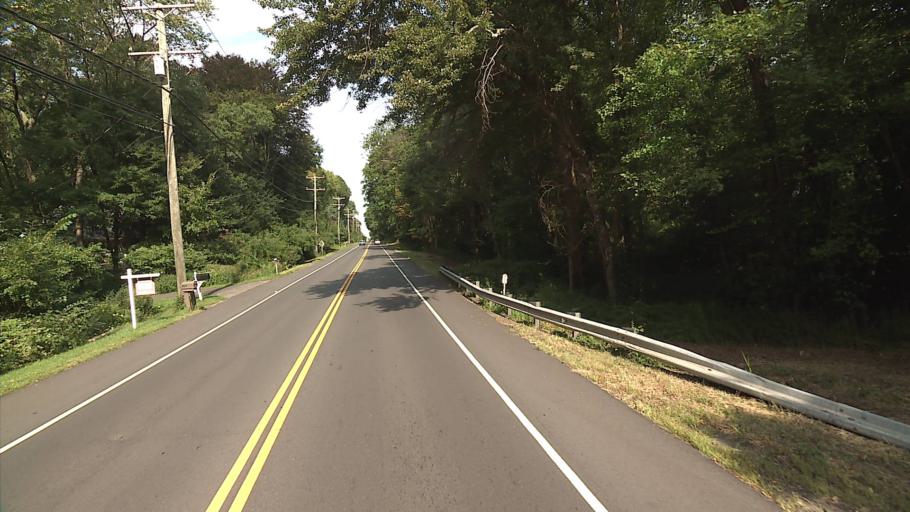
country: US
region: Connecticut
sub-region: Fairfield County
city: New Canaan
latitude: 41.1361
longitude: -73.4662
